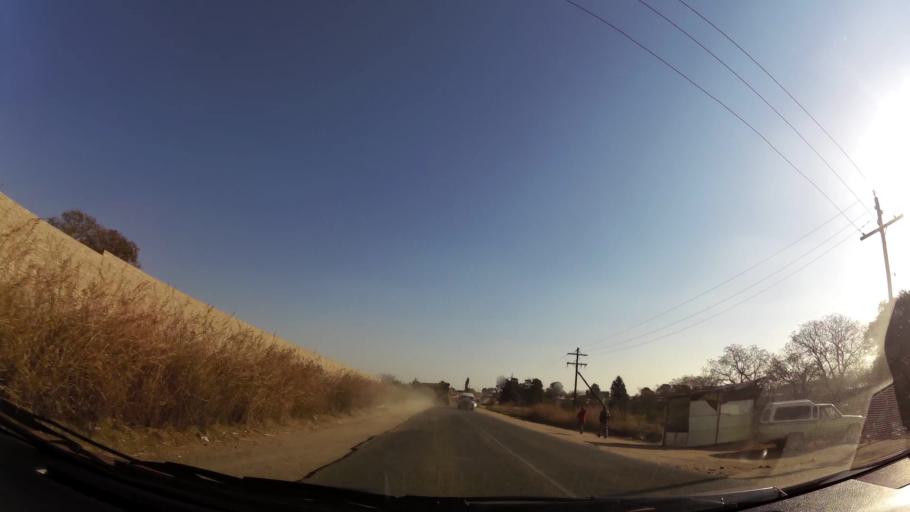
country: ZA
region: Gauteng
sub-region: West Rand District Municipality
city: Muldersdriseloop
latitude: -26.0228
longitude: 27.8749
